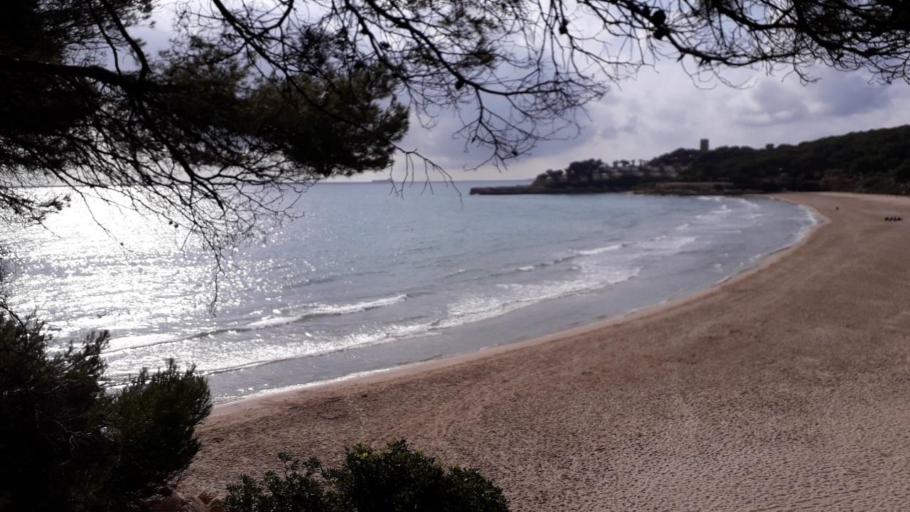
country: ES
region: Catalonia
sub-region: Provincia de Tarragona
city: Altafulla
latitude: 41.1285
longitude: 1.3491
